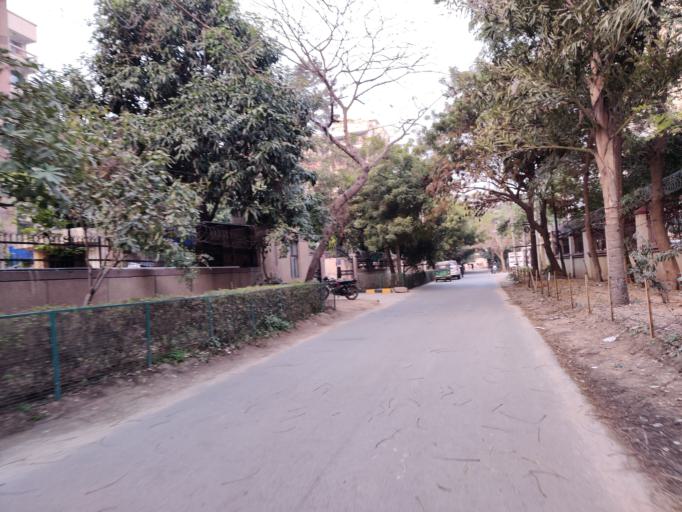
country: IN
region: Haryana
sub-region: Gurgaon
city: Gurgaon
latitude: 28.4424
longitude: 77.0633
